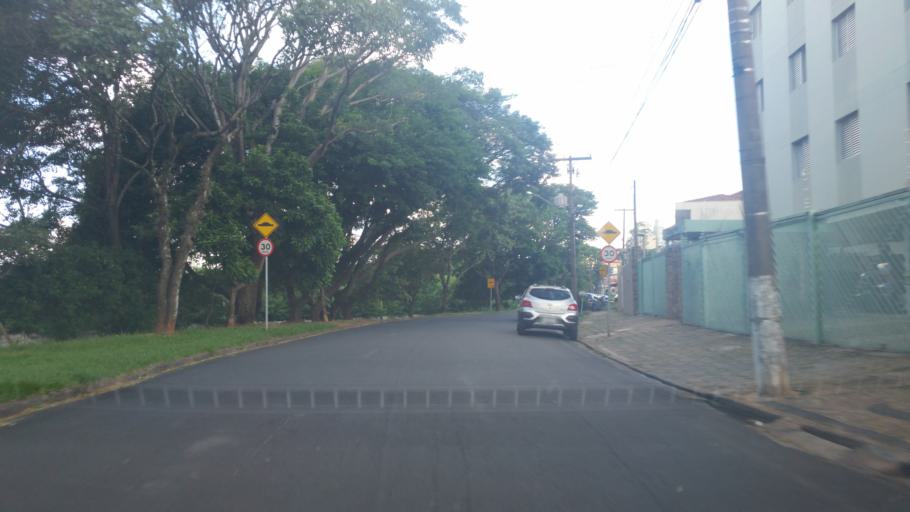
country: BR
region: Sao Paulo
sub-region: Campinas
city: Campinas
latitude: -22.8799
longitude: -47.0321
